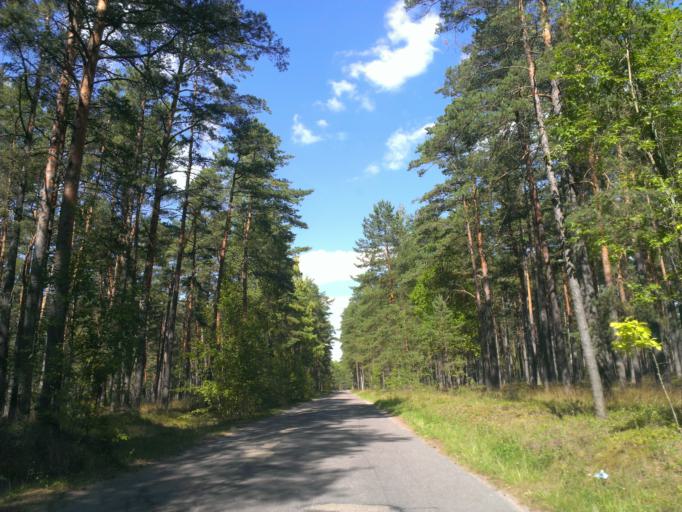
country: LV
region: Adazi
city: Adazi
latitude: 57.1191
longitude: 24.3455
